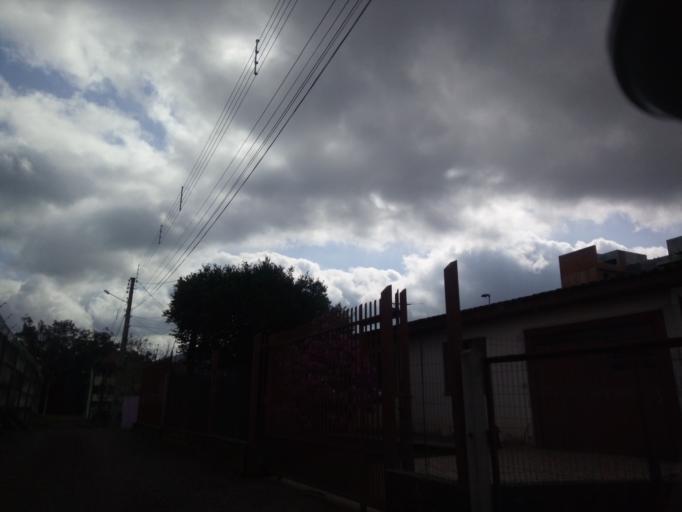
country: BR
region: Rio Grande do Sul
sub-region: Santa Maria
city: Santa Maria
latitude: -29.7021
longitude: -53.7269
